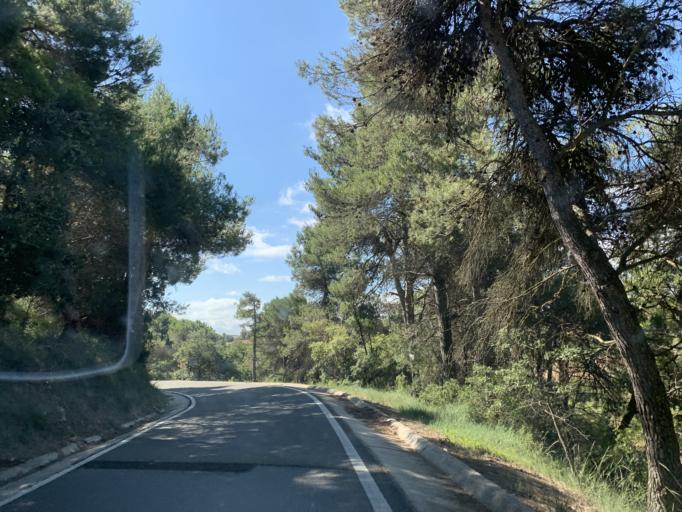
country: ES
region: Catalonia
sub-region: Provincia de Tarragona
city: Conesa
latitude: 41.5402
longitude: 1.3130
